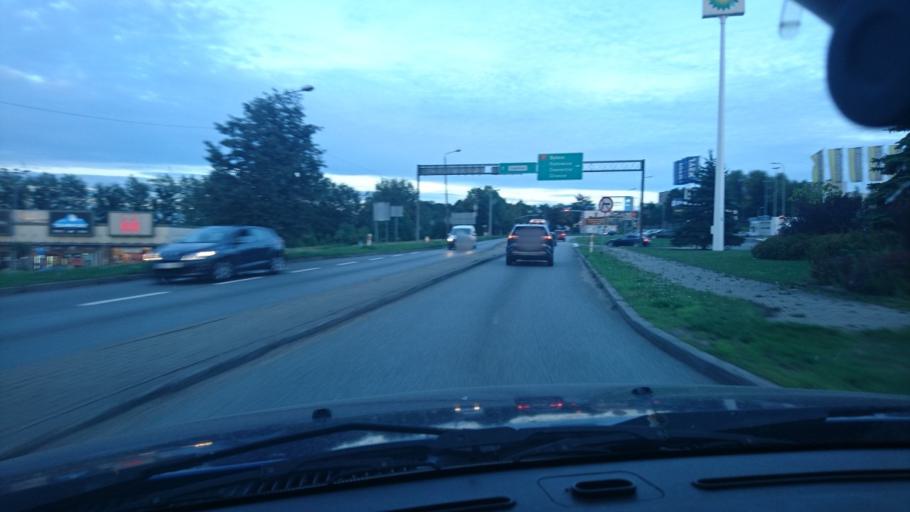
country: PL
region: Silesian Voivodeship
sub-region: Powiat tarnogorski
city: Tarnowskie Gory
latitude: 50.4543
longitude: 18.8367
